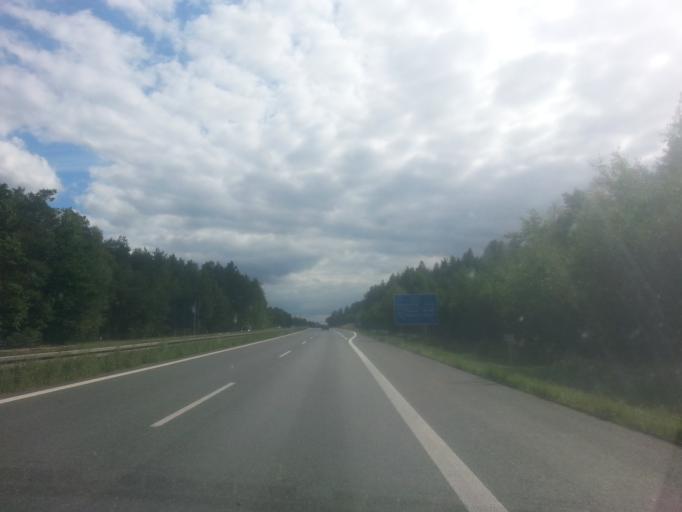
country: DE
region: Bavaria
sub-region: Upper Palatinate
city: Wackersdorf
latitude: 49.3347
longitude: 12.1509
